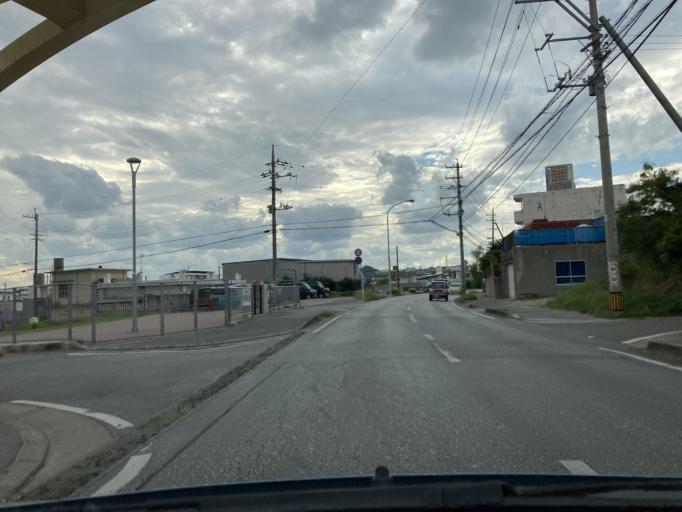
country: JP
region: Okinawa
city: Gushikawa
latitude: 26.3490
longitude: 127.8562
